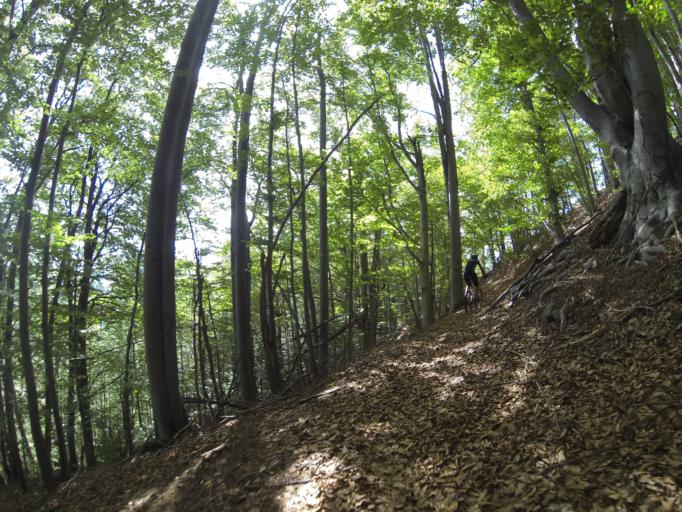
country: RO
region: Valcea
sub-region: Comuna Barbatesti
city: Barbatesti
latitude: 45.2483
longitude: 24.1644
